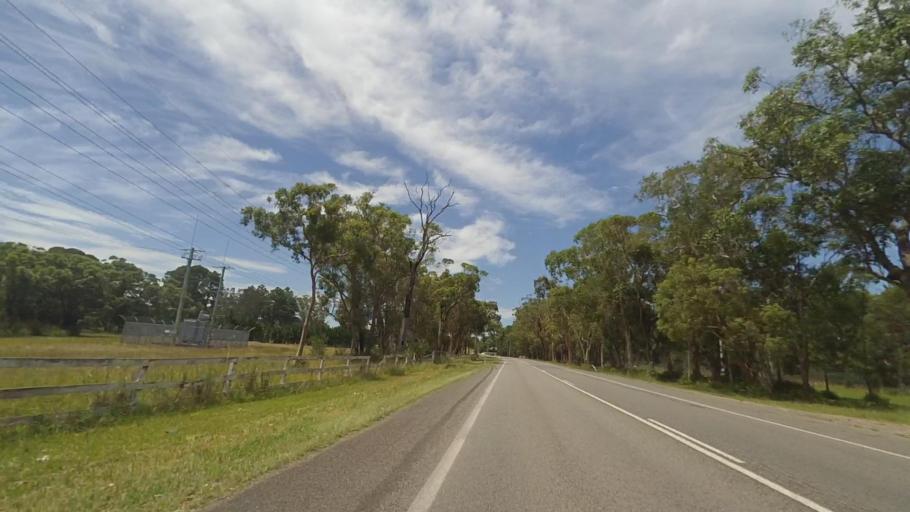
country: AU
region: New South Wales
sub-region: Port Stephens Shire
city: Medowie
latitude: -32.7669
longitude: 151.8634
